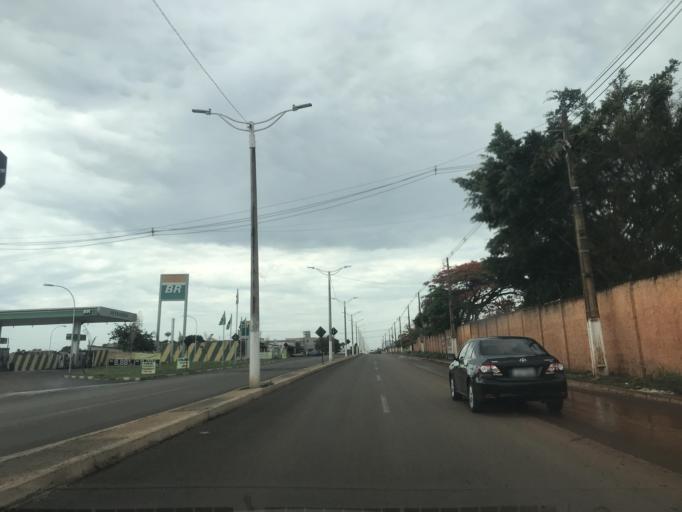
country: BR
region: Goias
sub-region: Luziania
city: Luziania
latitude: -16.2234
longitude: -47.9361
